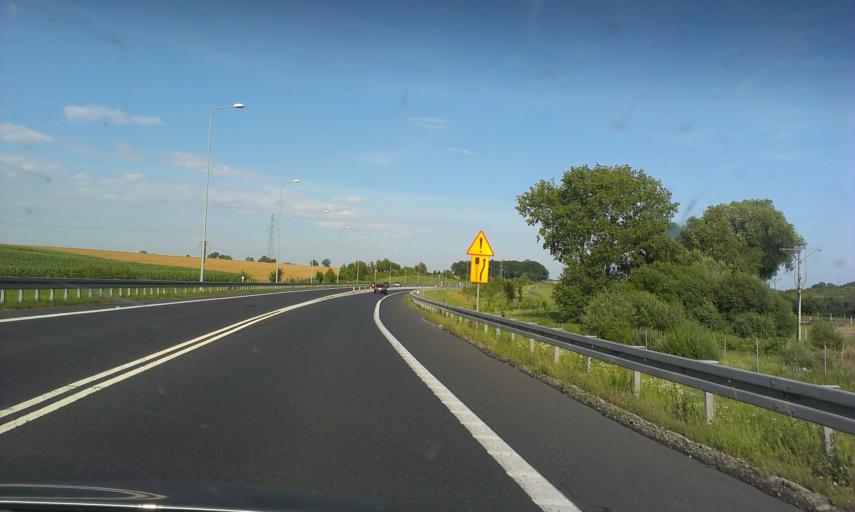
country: PL
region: Greater Poland Voivodeship
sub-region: Powiat pilski
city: Wyrzysk
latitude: 53.1623
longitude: 17.2087
